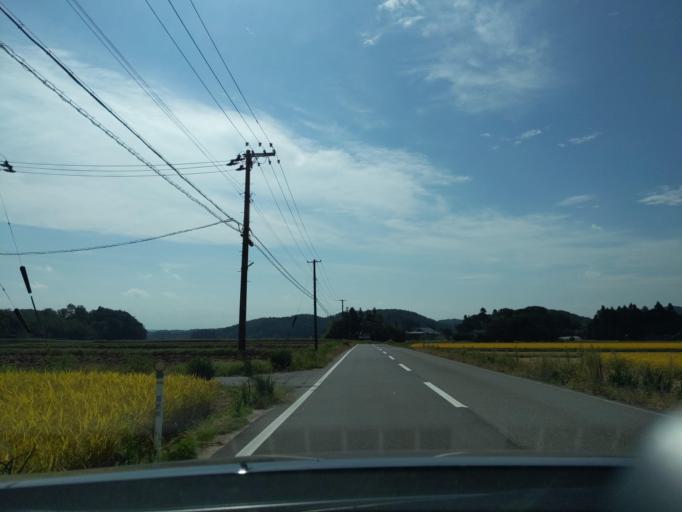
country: JP
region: Fukushima
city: Koriyama
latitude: 37.3805
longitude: 140.2628
